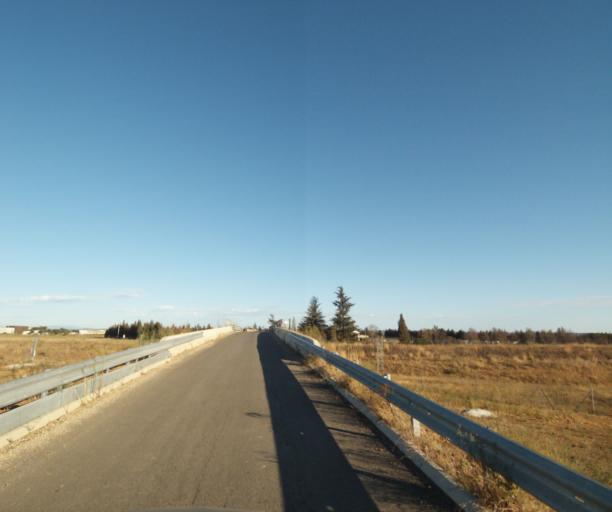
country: FR
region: Languedoc-Roussillon
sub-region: Departement du Gard
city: Bouillargues
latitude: 43.7877
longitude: 4.4478
